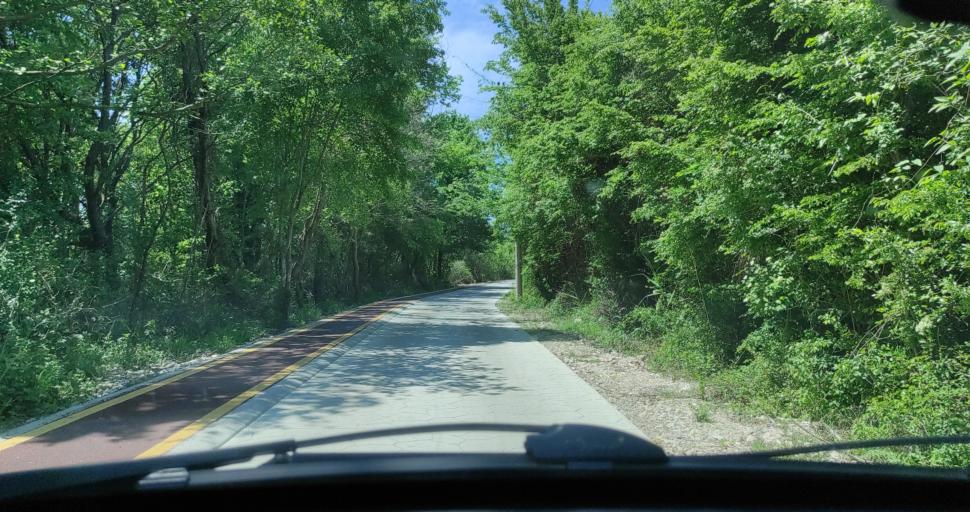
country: AL
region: Lezhe
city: Lezhe
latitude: 41.7483
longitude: 19.6034
